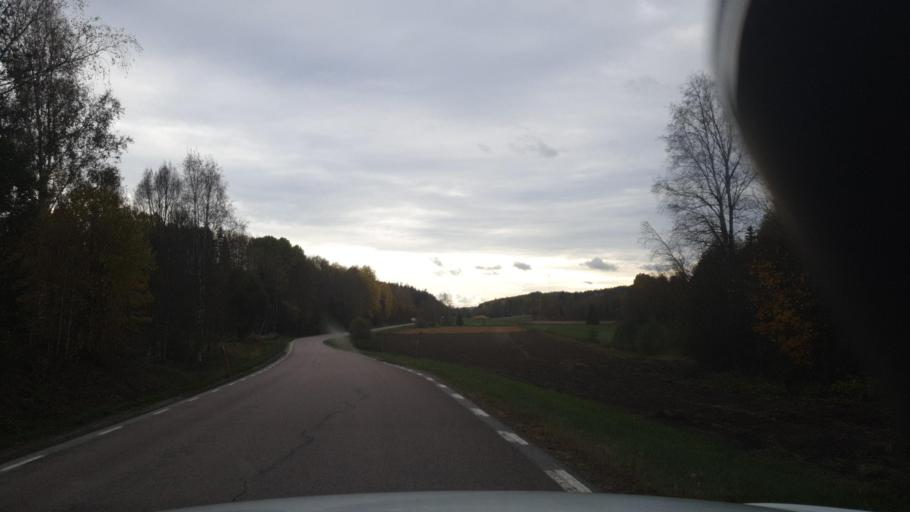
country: SE
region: Vaermland
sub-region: Arvika Kommun
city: Arvika
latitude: 59.6756
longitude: 12.7960
